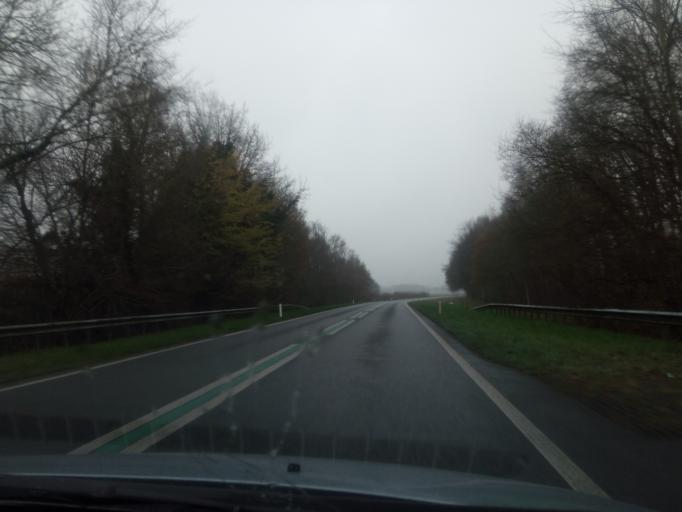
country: NL
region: Groningen
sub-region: Gemeente Vlagtwedde
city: Vlagtwedde
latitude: 53.0865
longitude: 7.0847
